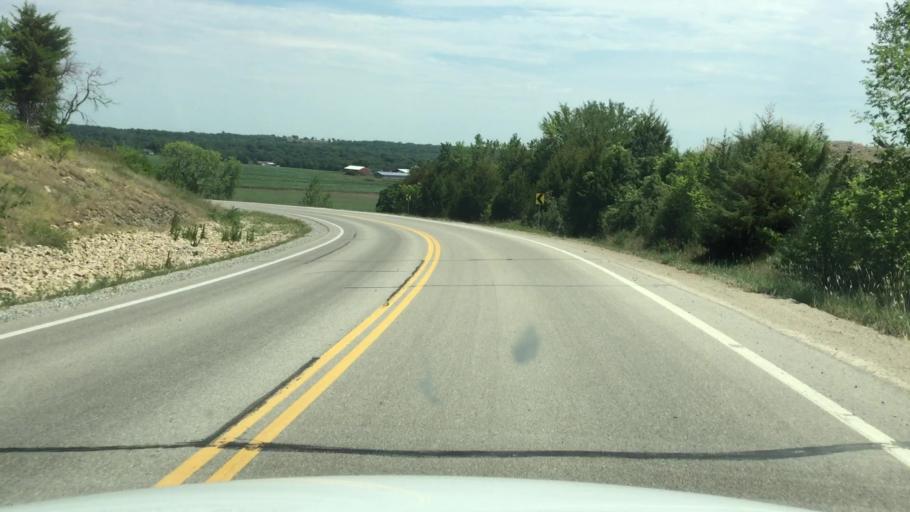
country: US
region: Kansas
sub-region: Shawnee County
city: Topeka
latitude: 38.9723
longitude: -95.4911
